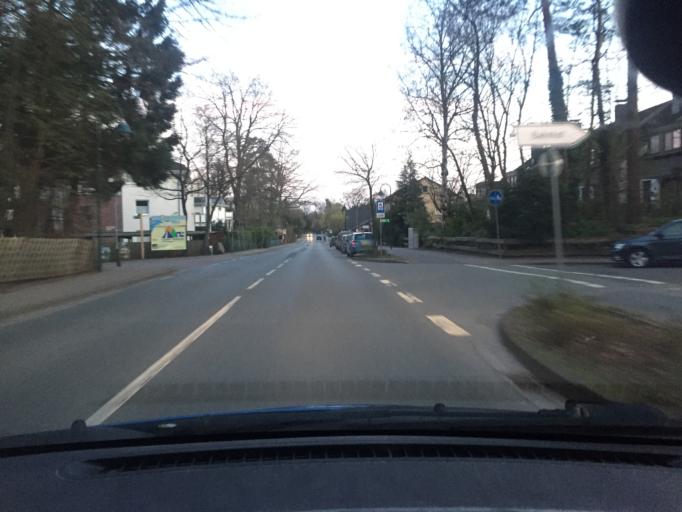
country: DE
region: Lower Saxony
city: Buchholz in der Nordheide
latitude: 53.2842
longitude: 9.8714
